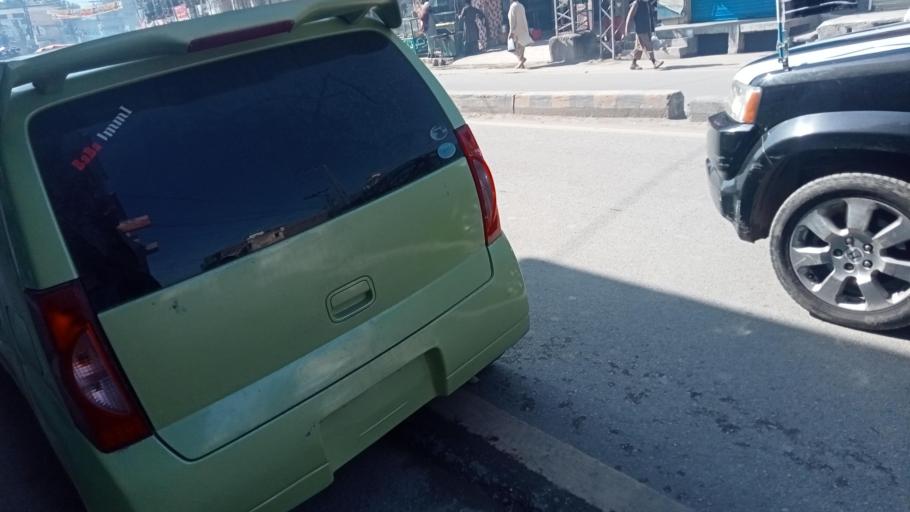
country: PK
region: Khyber Pakhtunkhwa
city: Mingora
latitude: 34.7681
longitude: 72.3600
